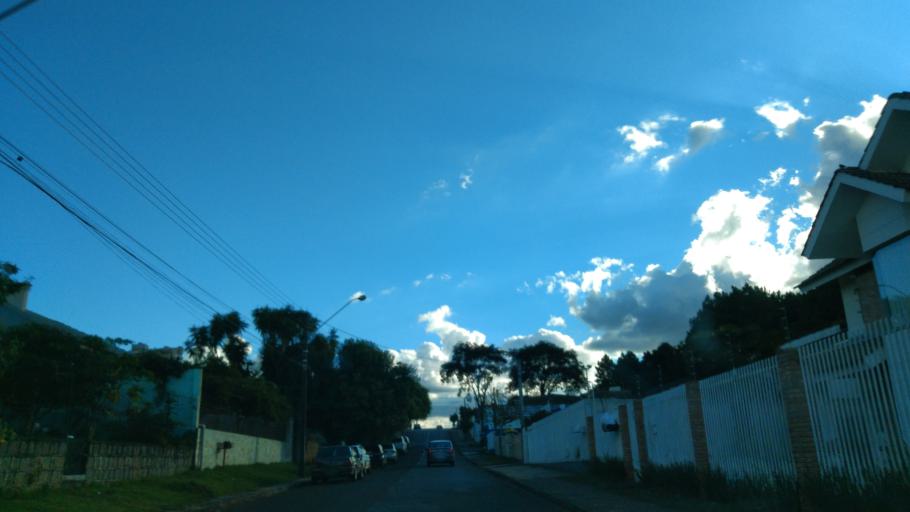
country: BR
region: Parana
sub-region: Guarapuava
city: Guarapuava
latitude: -25.3848
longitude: -51.4601
